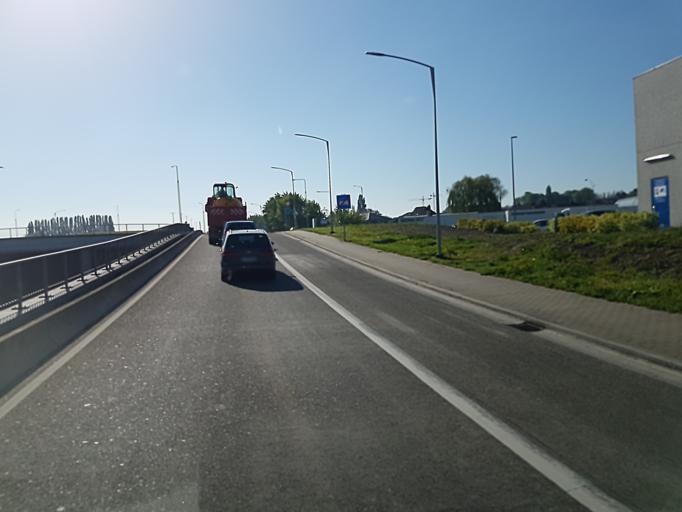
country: BE
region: Wallonia
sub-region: Province du Hainaut
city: Mouscron
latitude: 50.7447
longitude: 3.2342
